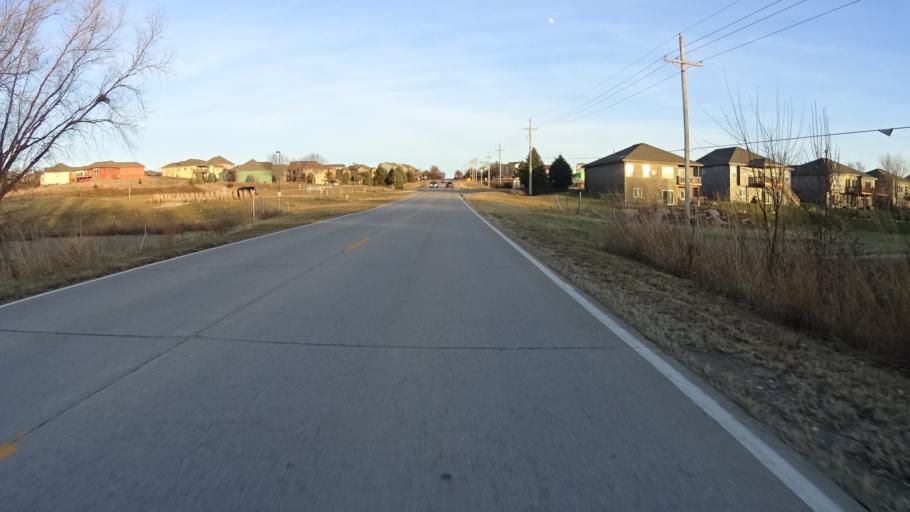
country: US
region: Nebraska
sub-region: Sarpy County
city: Papillion
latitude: 41.1326
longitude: -96.0656
